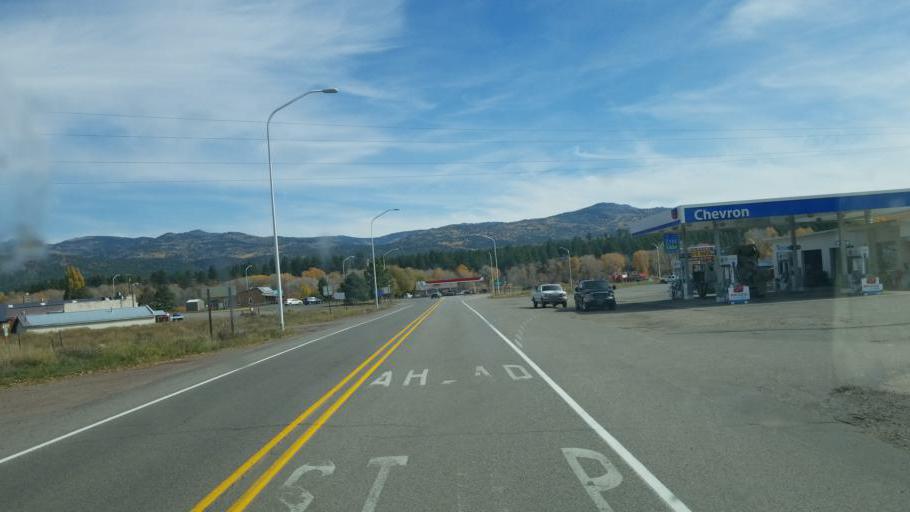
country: US
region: New Mexico
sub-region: Rio Arriba County
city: Chama
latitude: 36.8830
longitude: -106.5870
